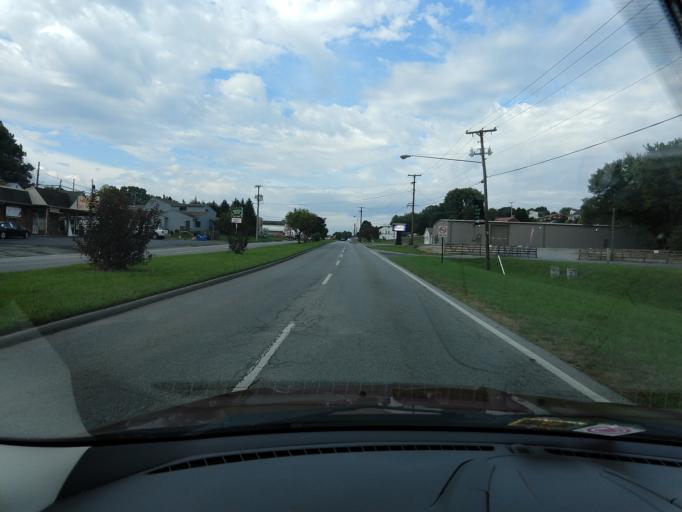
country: US
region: Virginia
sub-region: Roanoke County
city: Vinton
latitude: 37.2781
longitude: -79.8749
